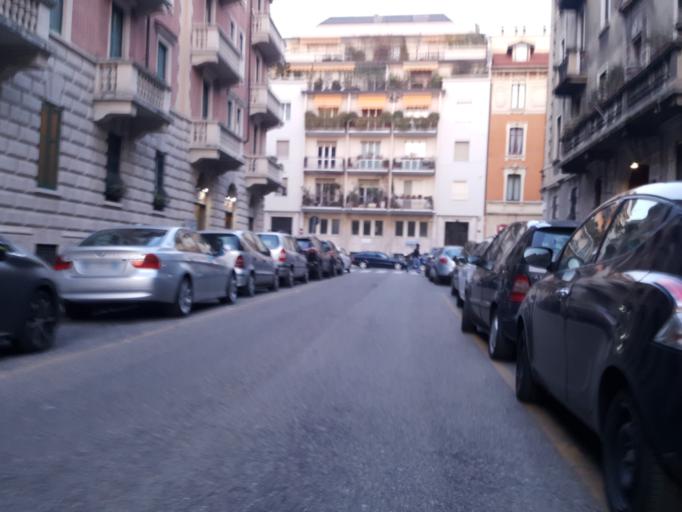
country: IT
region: Lombardy
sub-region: Citta metropolitana di Milano
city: Milano
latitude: 45.4620
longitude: 9.1616
